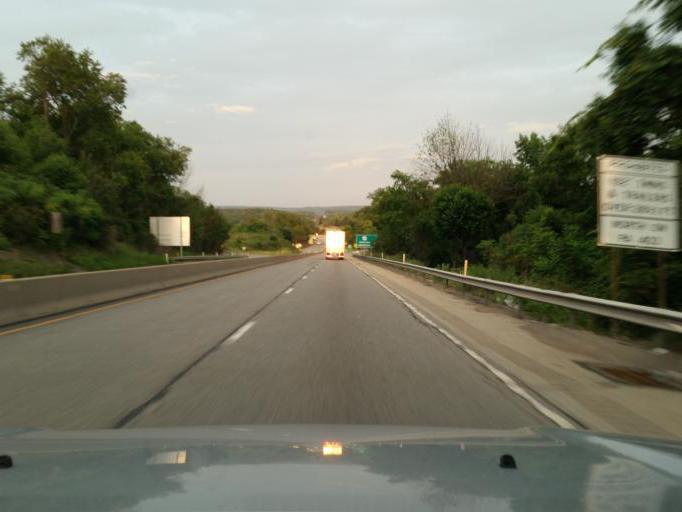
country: US
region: Pennsylvania
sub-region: Cambria County
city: Westmont
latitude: 40.4568
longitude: -79.0164
